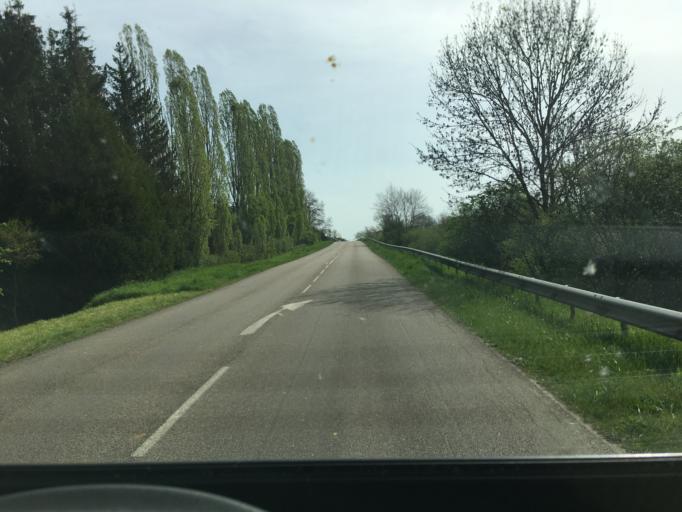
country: FR
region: Lorraine
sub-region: Departement de Meurthe-et-Moselle
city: Messein
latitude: 48.6113
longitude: 6.1311
